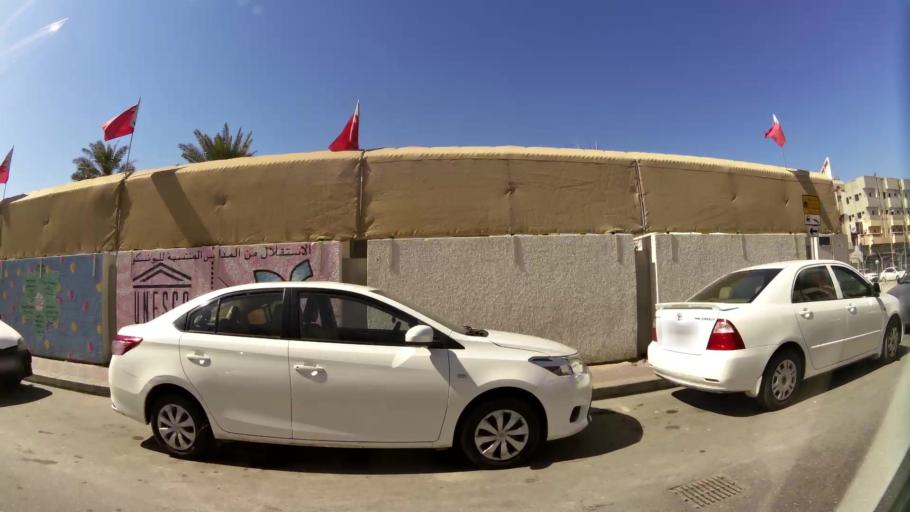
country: BH
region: Muharraq
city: Al Muharraq
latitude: 26.2472
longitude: 50.6095
